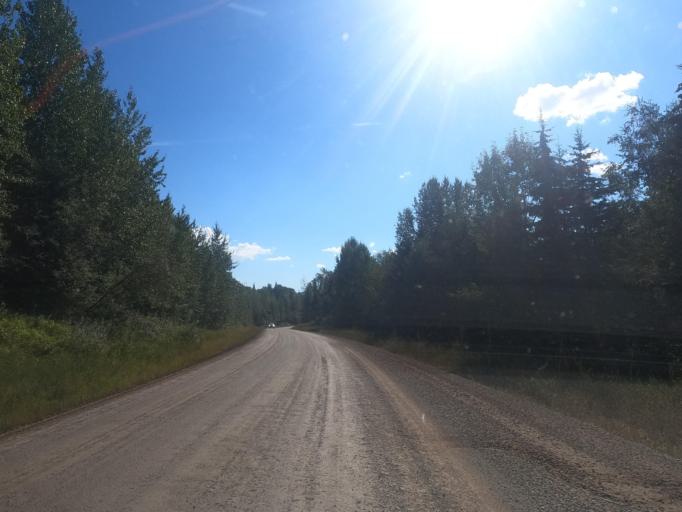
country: CA
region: British Columbia
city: Houston
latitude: 54.2952
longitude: -126.8458
